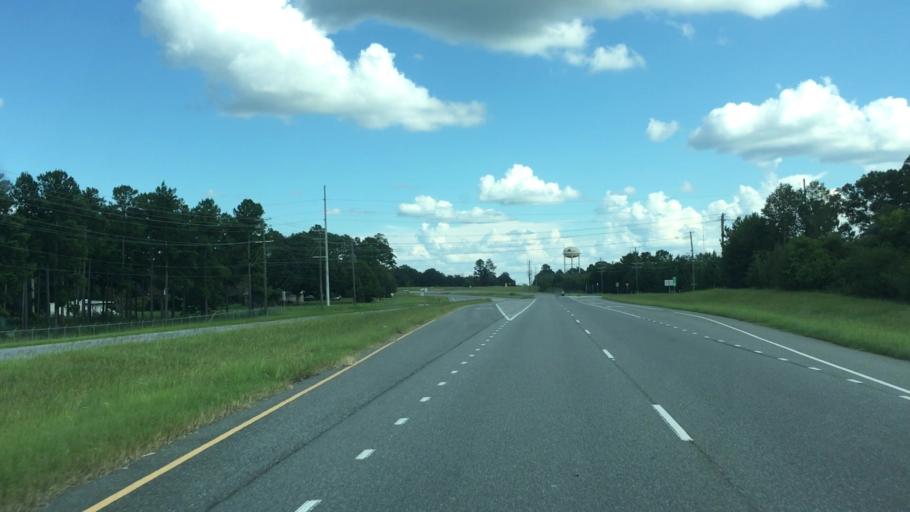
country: US
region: Georgia
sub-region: Laurens County
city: Dublin
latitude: 32.5052
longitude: -82.9445
